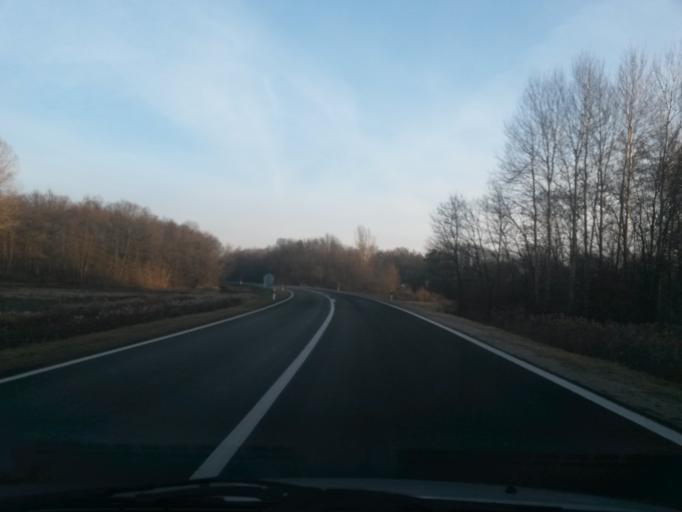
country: HR
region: Varazdinska
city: Jalzabet
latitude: 46.2821
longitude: 16.4869
